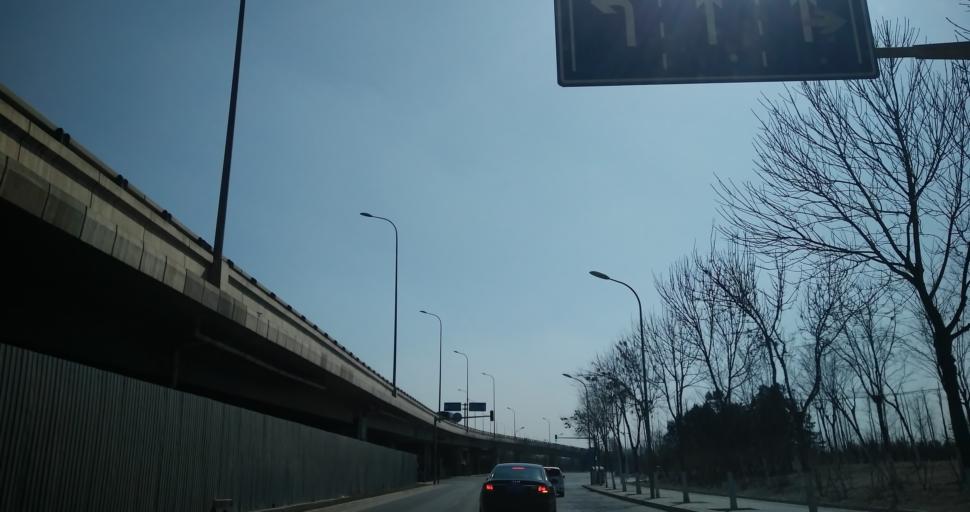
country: CN
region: Beijing
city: Jiugong
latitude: 39.7883
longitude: 116.4241
